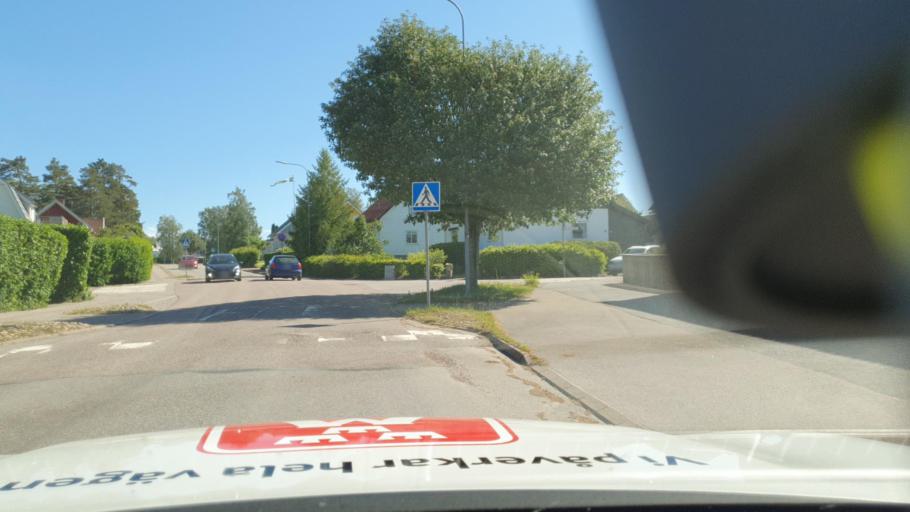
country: SE
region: Vaermland
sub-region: Kristinehamns Kommun
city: Kristinehamn
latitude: 59.3042
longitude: 14.0893
